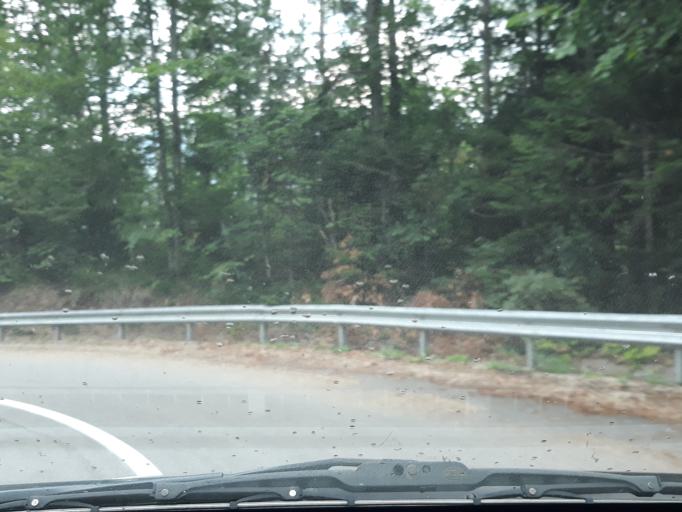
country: RO
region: Bihor
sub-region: Comuna Pietroasa
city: Pietroasa
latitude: 46.5983
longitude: 22.6694
